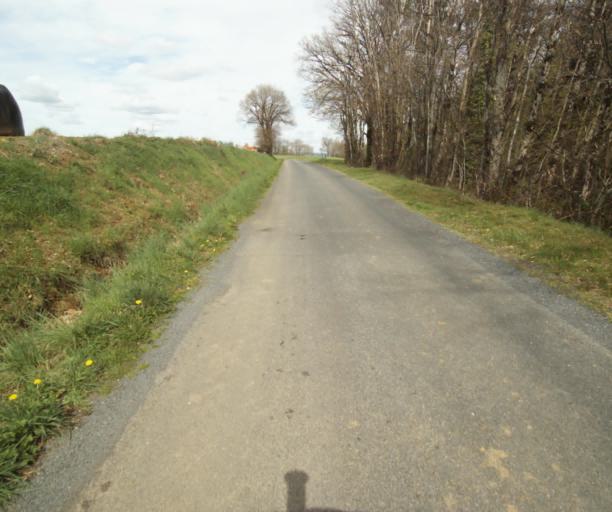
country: FR
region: Limousin
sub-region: Departement de la Correze
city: Laguenne
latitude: 45.2139
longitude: 1.8548
